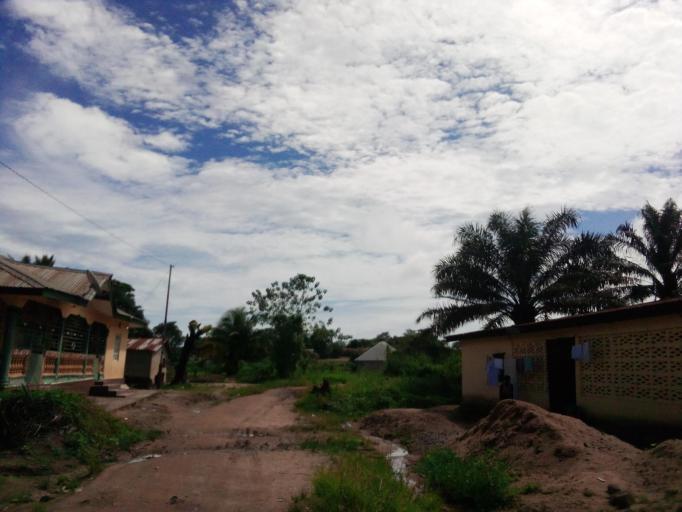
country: SL
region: Eastern Province
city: Koidu
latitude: 8.6526
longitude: -10.9603
